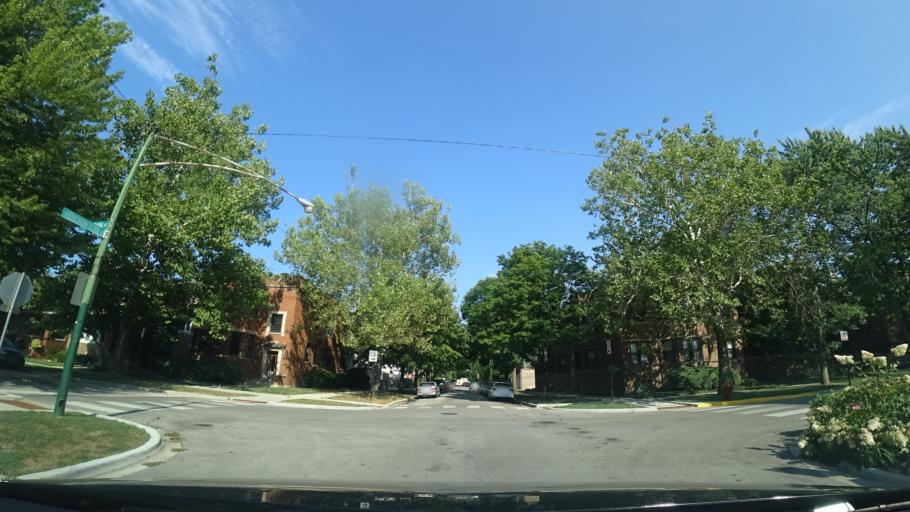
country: US
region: Illinois
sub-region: Cook County
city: Lincolnwood
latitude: 41.9776
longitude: -87.7126
